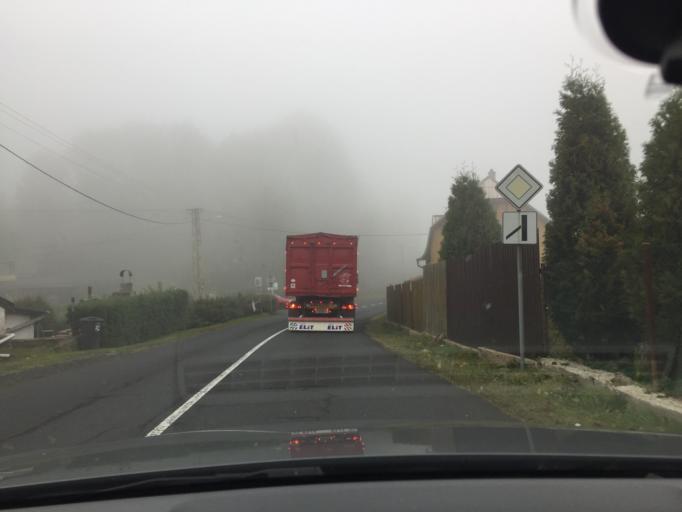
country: CZ
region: Ustecky
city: Libouchec
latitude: 50.7849
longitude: 13.9790
